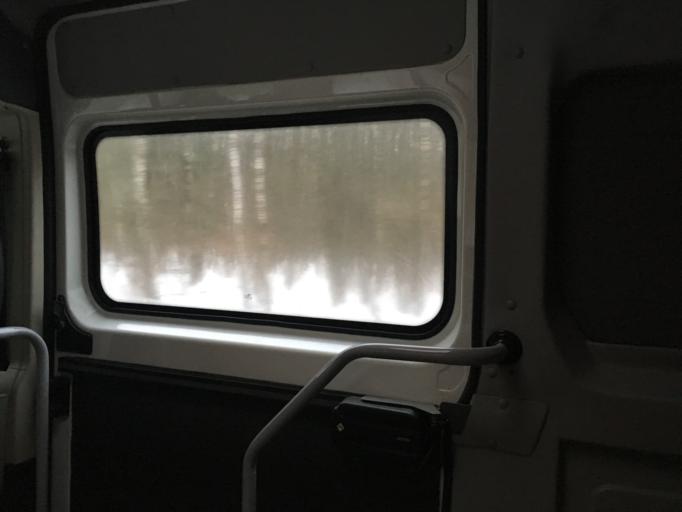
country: RU
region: Tula
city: Krapivna
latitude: 54.1270
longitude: 37.2483
